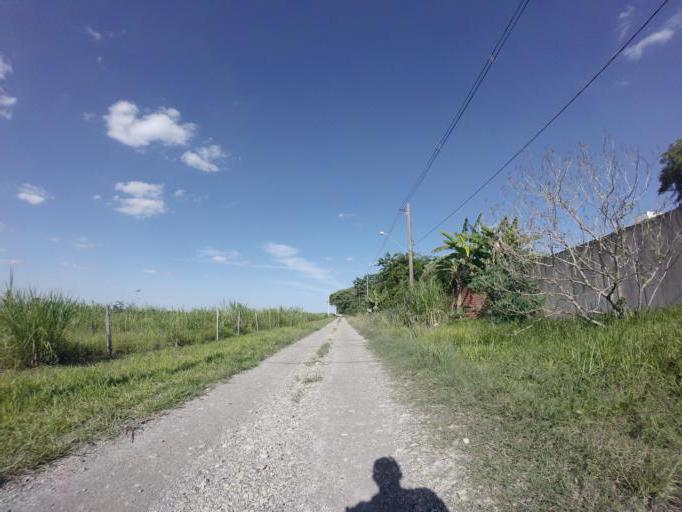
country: BR
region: Sao Paulo
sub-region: Piracicaba
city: Piracicaba
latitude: -22.7496
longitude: -47.5895
